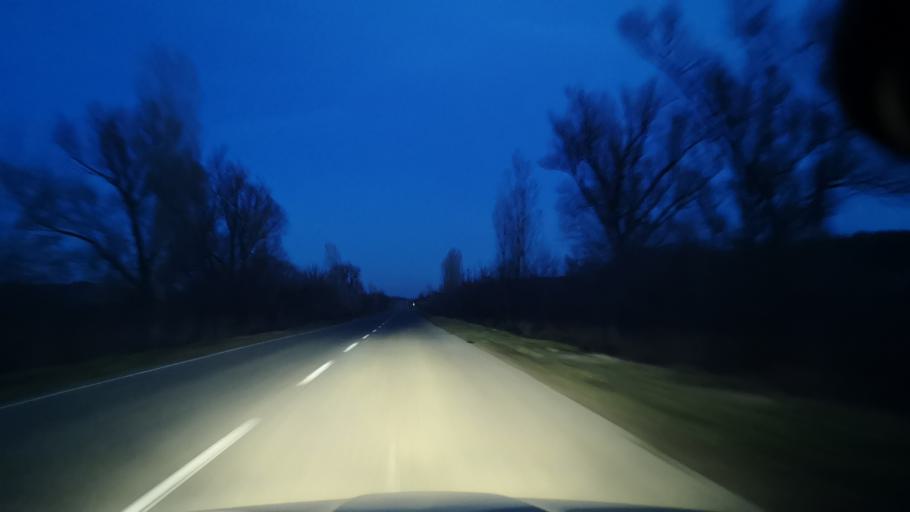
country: MD
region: Orhei
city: Orhei
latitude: 47.3444
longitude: 28.7121
